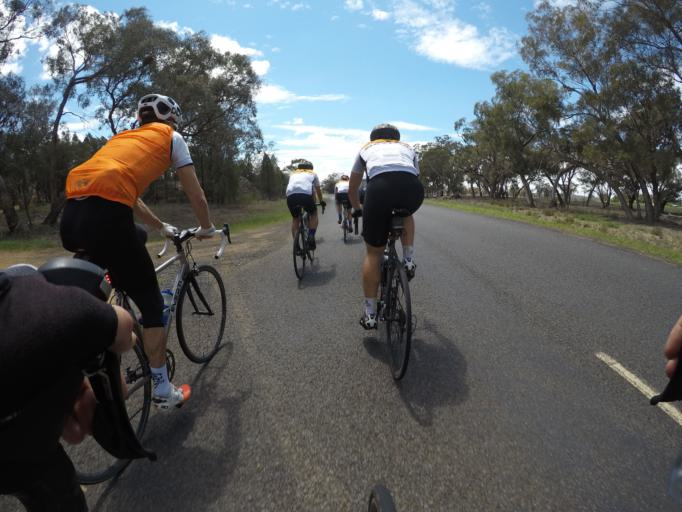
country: AU
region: New South Wales
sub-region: Dubbo Municipality
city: Dubbo
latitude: -32.3446
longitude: 148.5992
